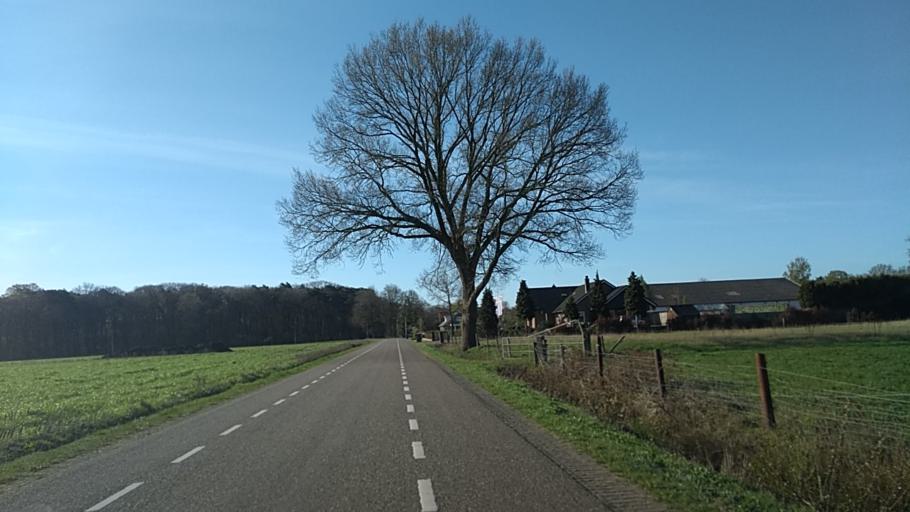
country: NL
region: Overijssel
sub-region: Gemeente Hof van Twente
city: Delden
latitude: 52.2612
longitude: 6.6731
